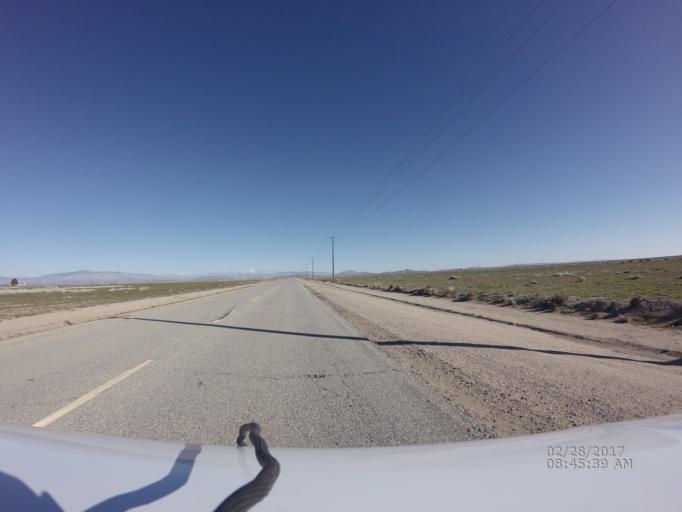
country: US
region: California
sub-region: Los Angeles County
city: Lancaster
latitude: 34.7654
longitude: -118.2372
